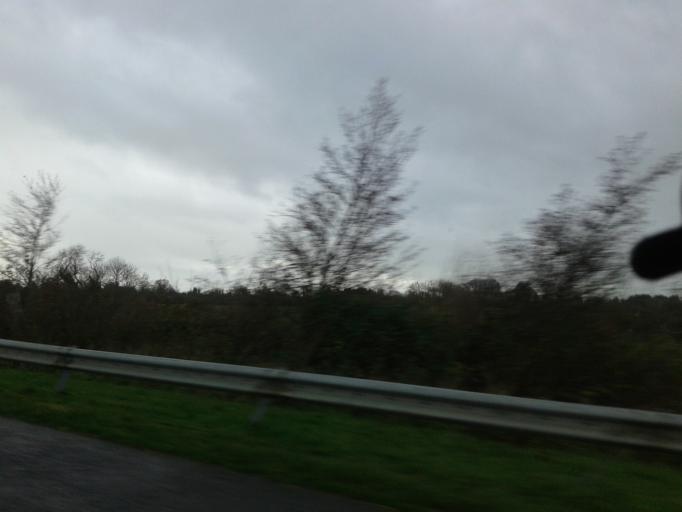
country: IE
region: Leinster
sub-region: An Mhi
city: Ashbourne
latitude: 53.5016
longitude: -6.4184
